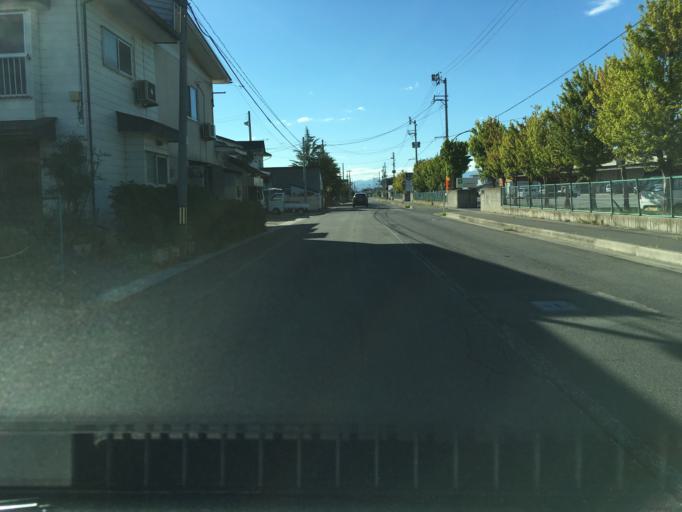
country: JP
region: Yamagata
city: Takahata
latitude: 37.9875
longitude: 140.1496
